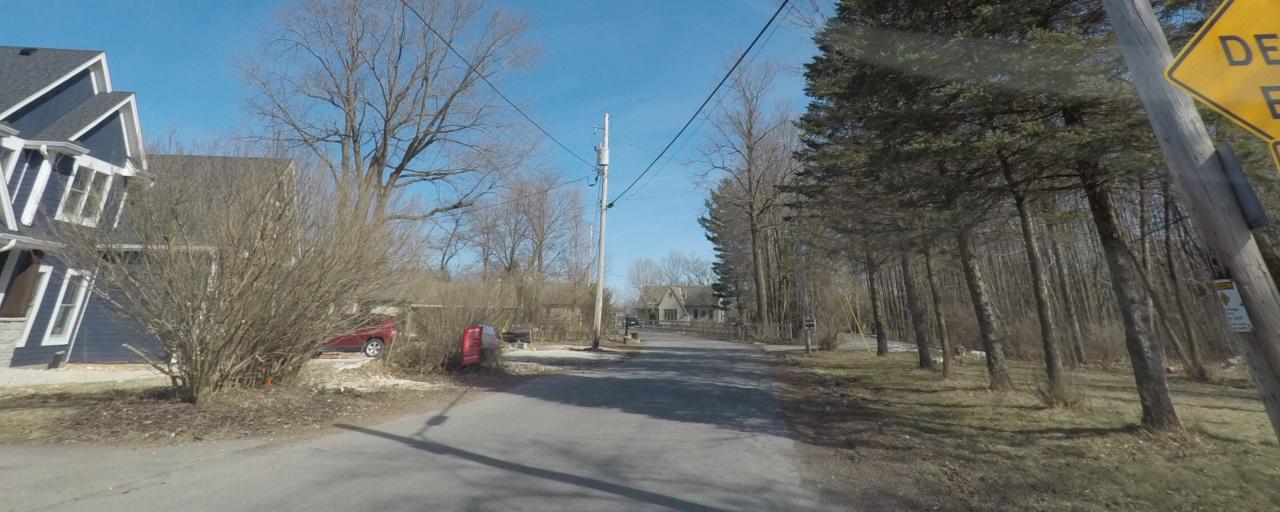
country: US
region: Wisconsin
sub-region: Waukesha County
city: Merton
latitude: 43.1619
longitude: -88.3211
